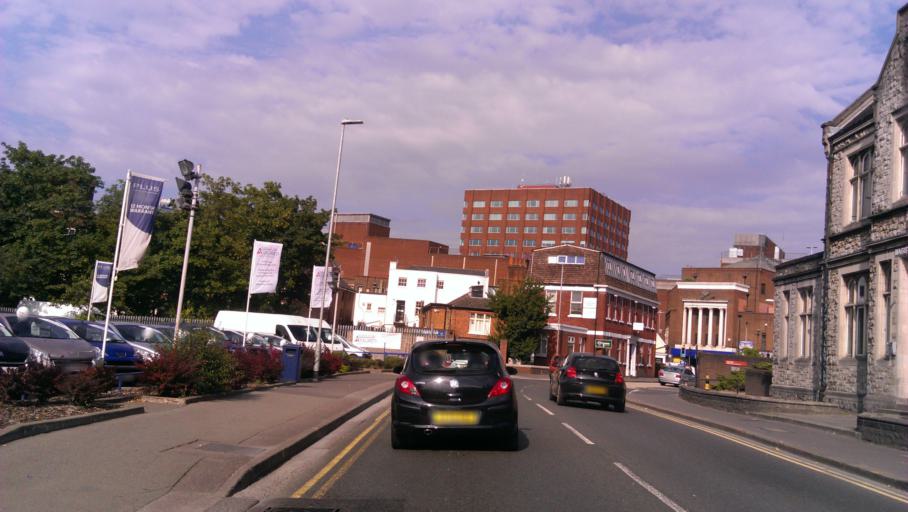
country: GB
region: England
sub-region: Kent
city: Maidstone
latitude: 51.2720
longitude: 0.5228
